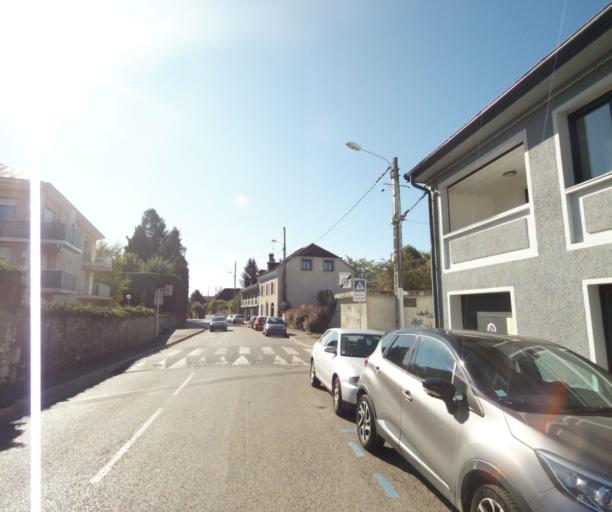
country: FR
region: Rhone-Alpes
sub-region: Departement de l'Ain
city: Ferney-Voltaire
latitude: 46.2549
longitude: 6.1118
